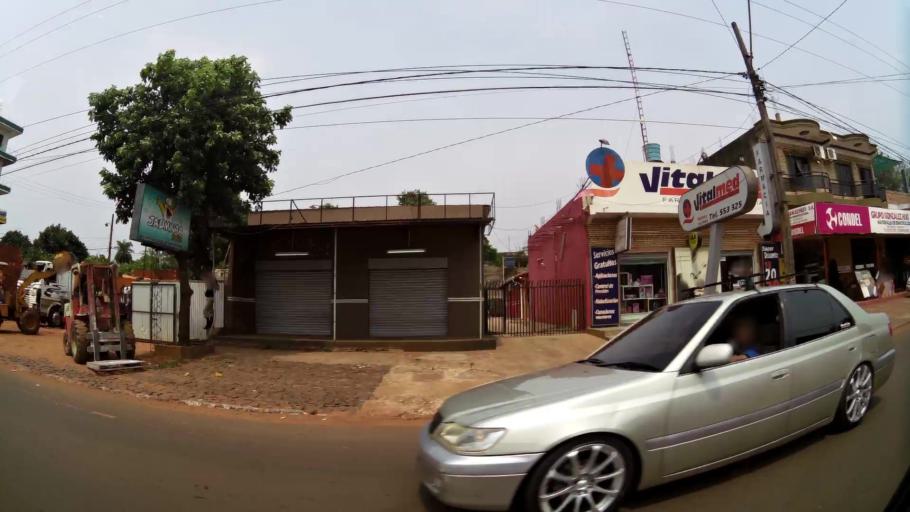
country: BR
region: Parana
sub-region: Foz Do Iguacu
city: Foz do Iguacu
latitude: -25.5635
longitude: -54.6125
